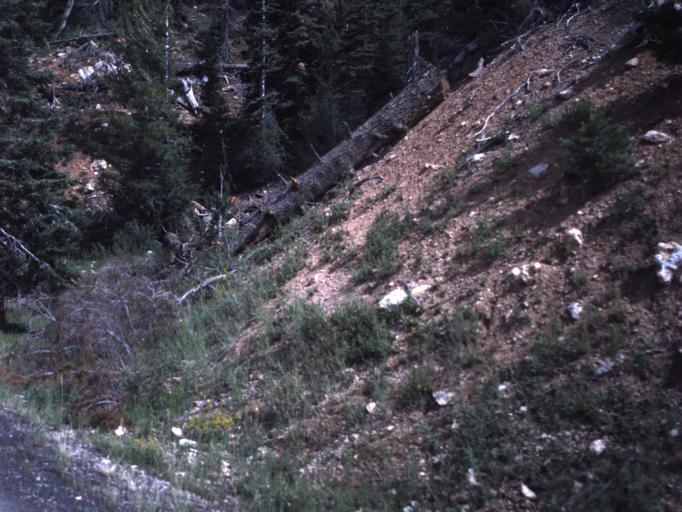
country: US
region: Utah
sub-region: Iron County
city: Cedar City
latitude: 37.5765
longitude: -112.8639
